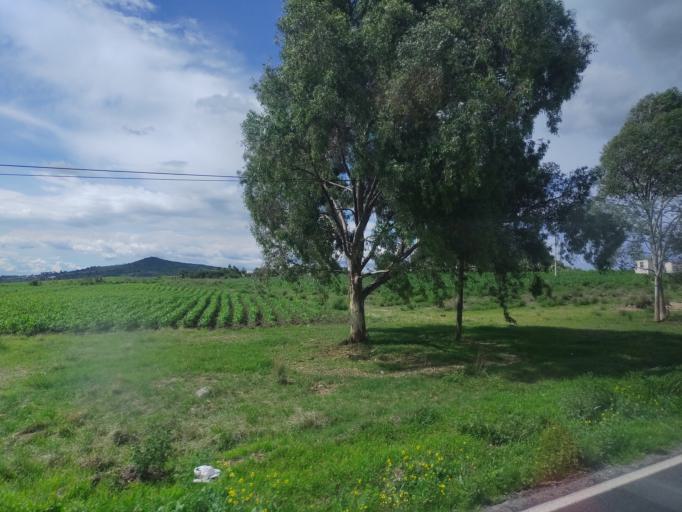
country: MX
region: Mexico
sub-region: Aculco
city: El Colorado
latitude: 20.0959
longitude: -99.7530
